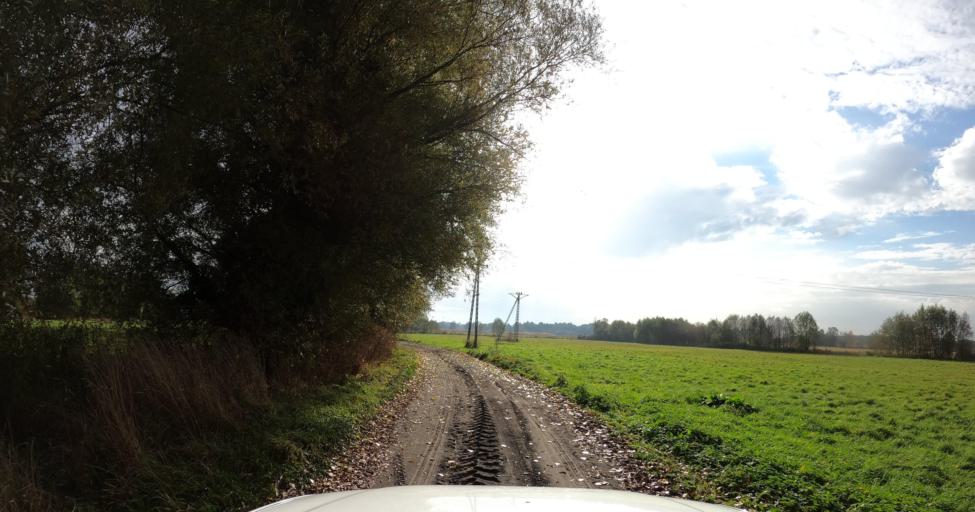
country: PL
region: West Pomeranian Voivodeship
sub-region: Powiat kamienski
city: Kamien Pomorski
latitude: 53.9905
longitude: 14.8444
